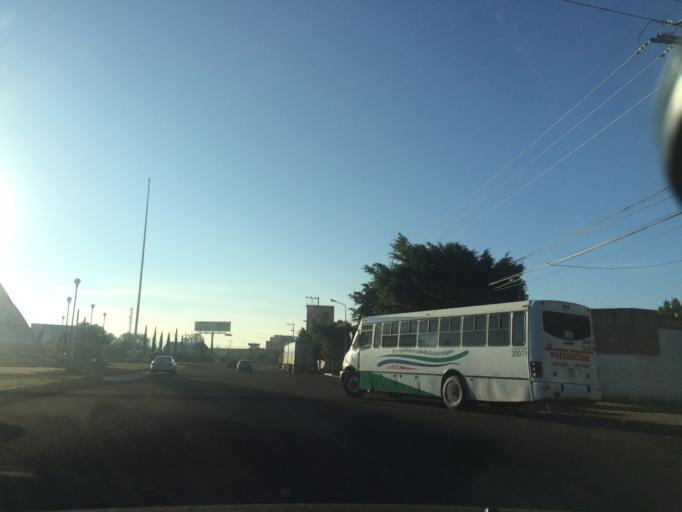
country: MX
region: Puebla
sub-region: Santiago Miahuatlan
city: San Jose Monte Chiquito
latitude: 18.4739
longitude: -97.4291
